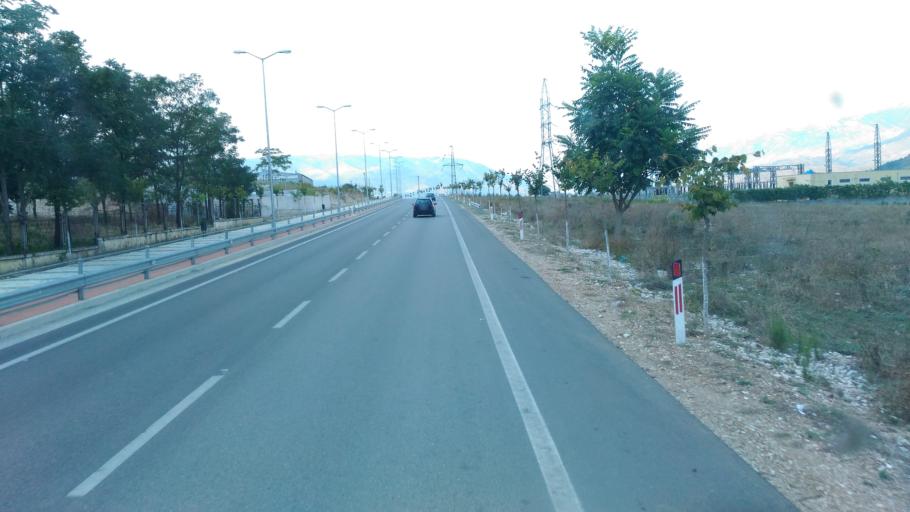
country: AL
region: Gjirokaster
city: Gjirokaster
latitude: 40.0917
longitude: 20.1370
